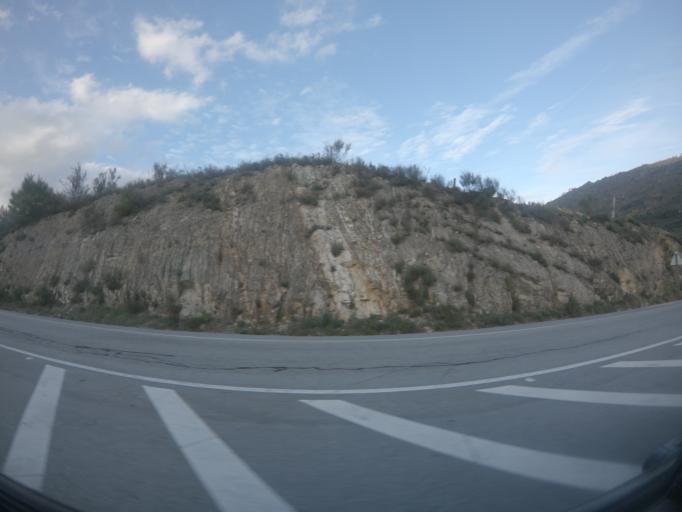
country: PT
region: Braganca
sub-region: Carrazeda de Ansiaes
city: Carrazeda de Anciaes
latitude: 41.2948
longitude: -7.3419
